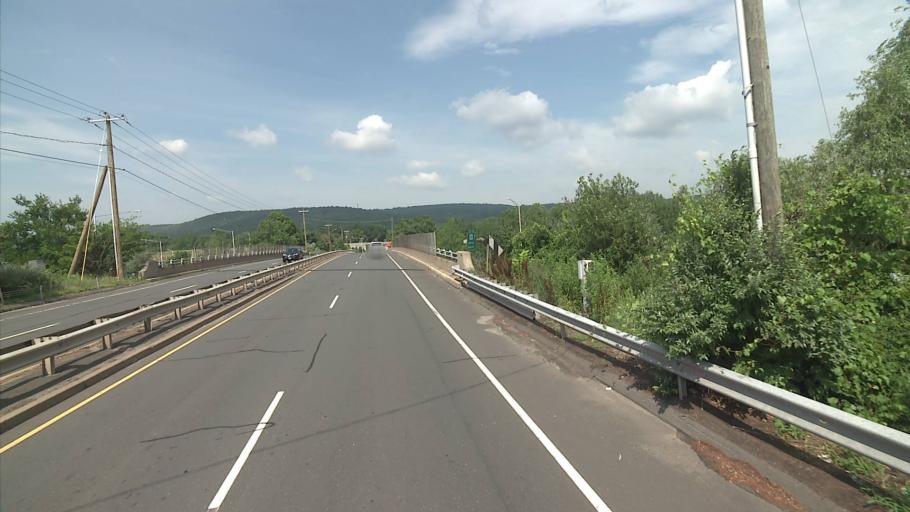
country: US
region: Connecticut
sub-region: New Haven County
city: Cheshire Village
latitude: 41.5635
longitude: -72.9132
